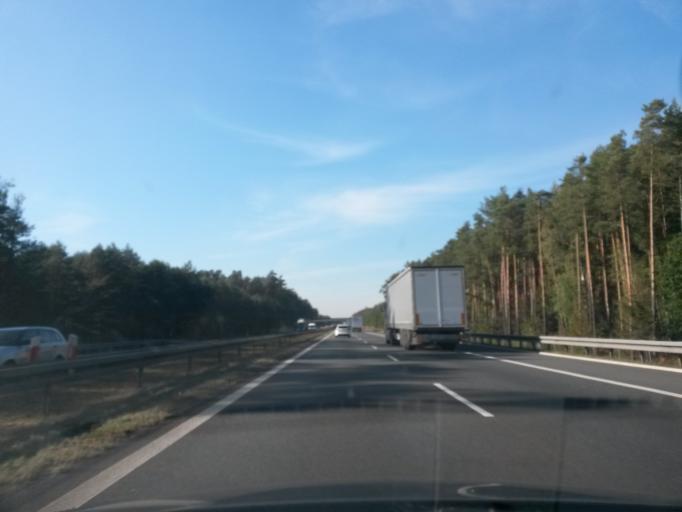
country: PL
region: Opole Voivodeship
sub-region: Powiat opolski
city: Komprachcice
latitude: 50.6195
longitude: 17.7635
